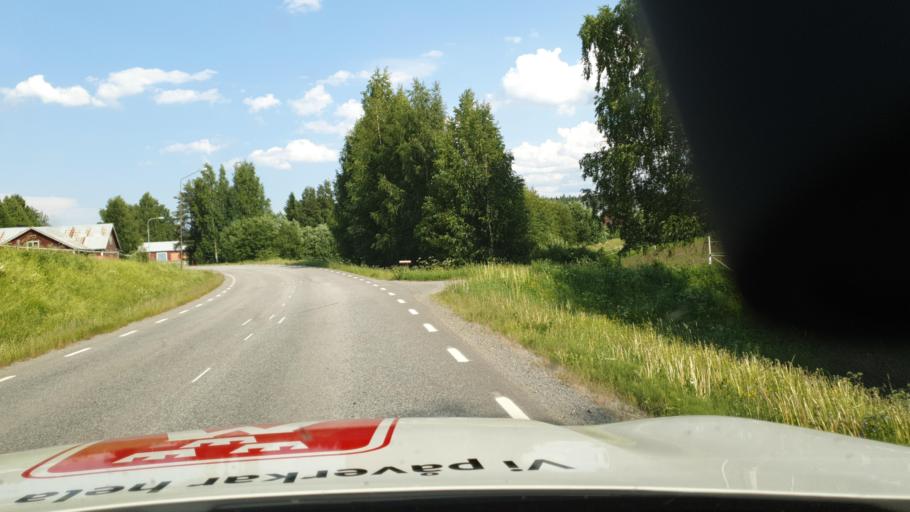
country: SE
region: Vaesterbotten
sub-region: Skelleftea Kommun
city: Viken
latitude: 64.7461
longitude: 20.8503
